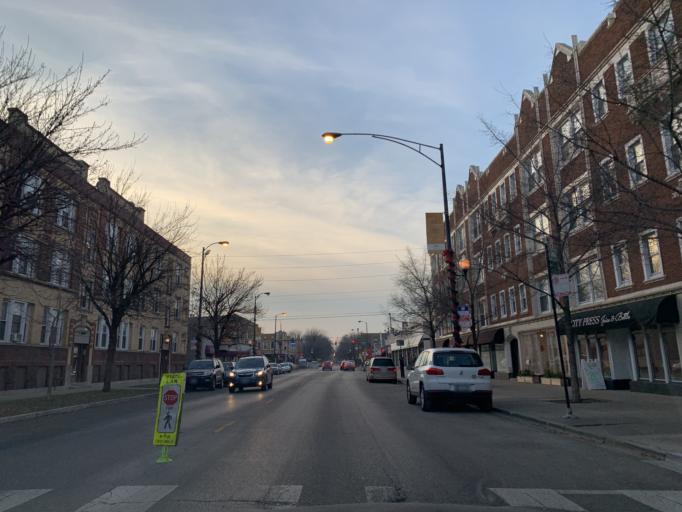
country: US
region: Illinois
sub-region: Cook County
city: Lincolnwood
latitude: 41.9615
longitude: -87.6776
